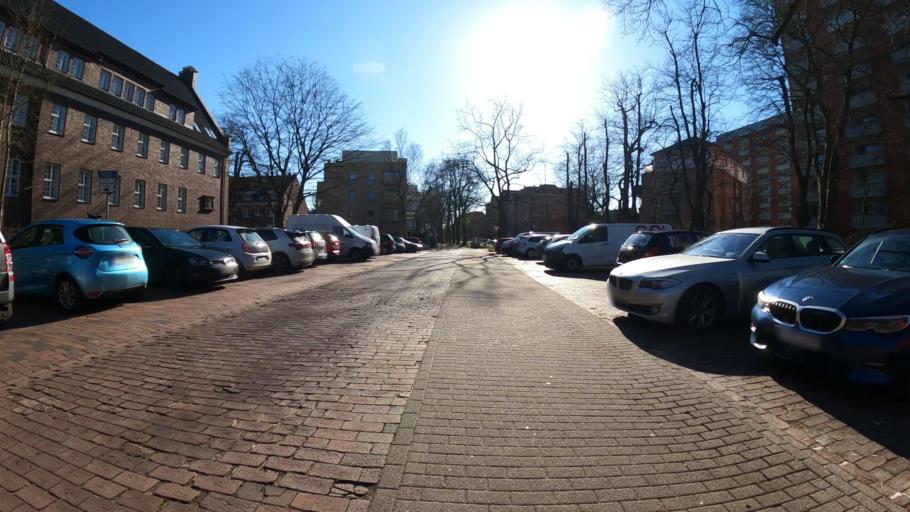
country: DE
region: Schleswig-Holstein
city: Pinneberg
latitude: 53.6593
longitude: 9.7970
